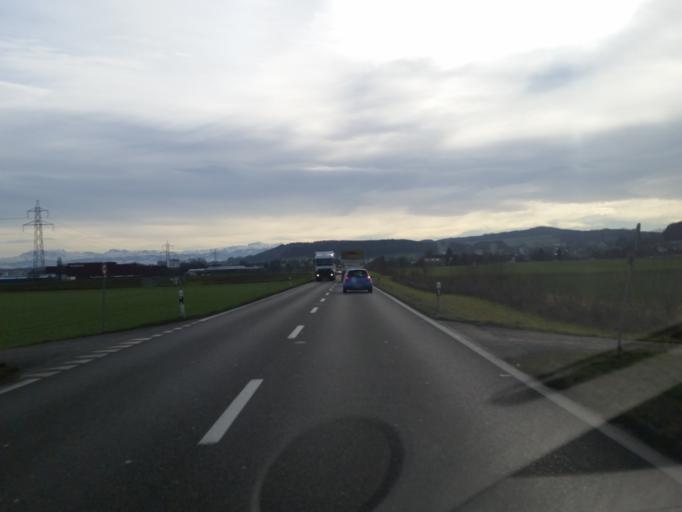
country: CH
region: Aargau
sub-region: Bezirk Bremgarten
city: Villmergen
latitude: 47.3645
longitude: 8.2367
